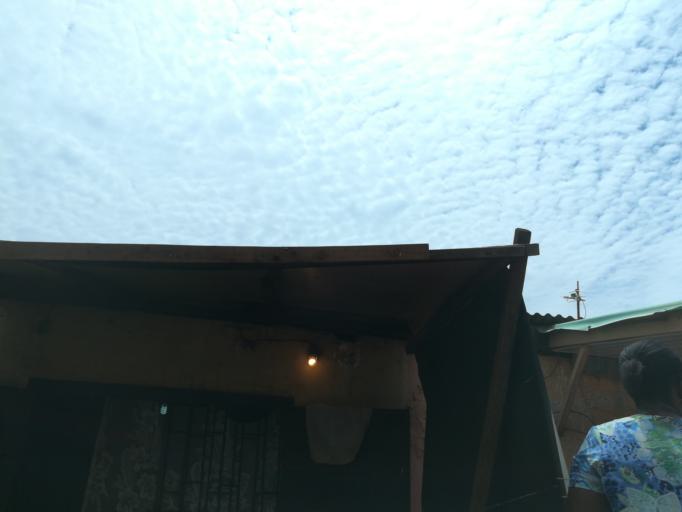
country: NG
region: Lagos
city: Oshodi
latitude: 6.5617
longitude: 3.3303
